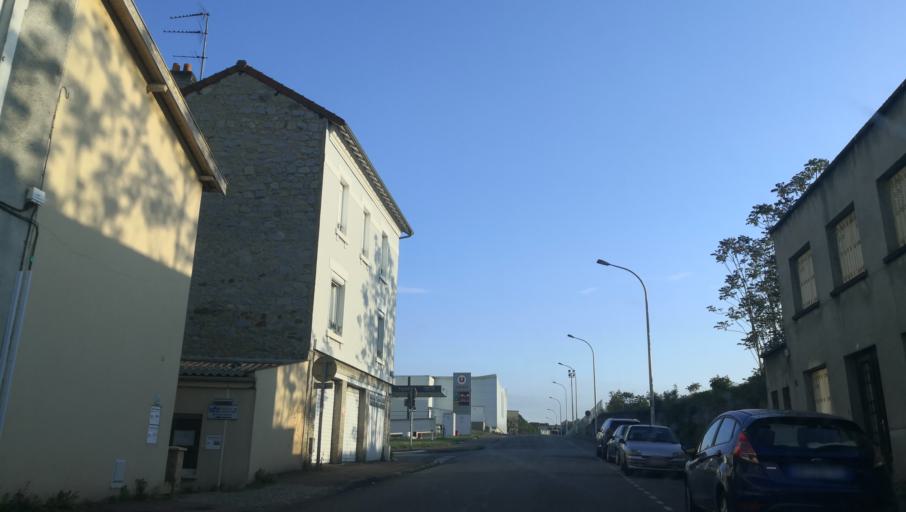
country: FR
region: Limousin
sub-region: Departement de la Haute-Vienne
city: Limoges
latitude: 45.8411
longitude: 1.2539
